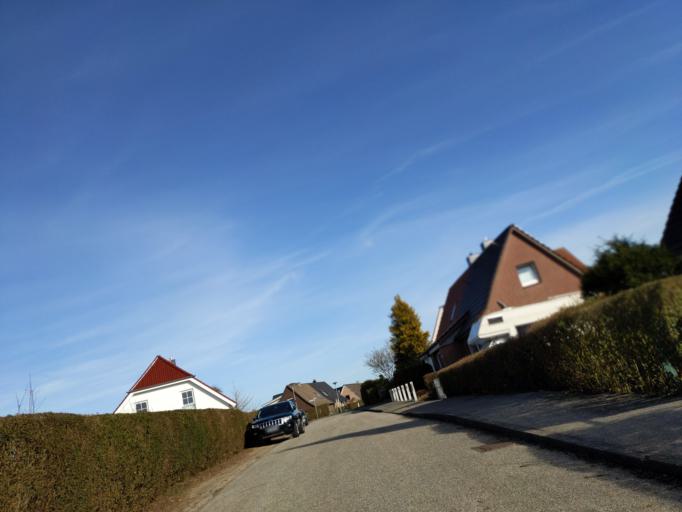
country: DE
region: Schleswig-Holstein
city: Travemuende
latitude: 53.9553
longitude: 10.8490
